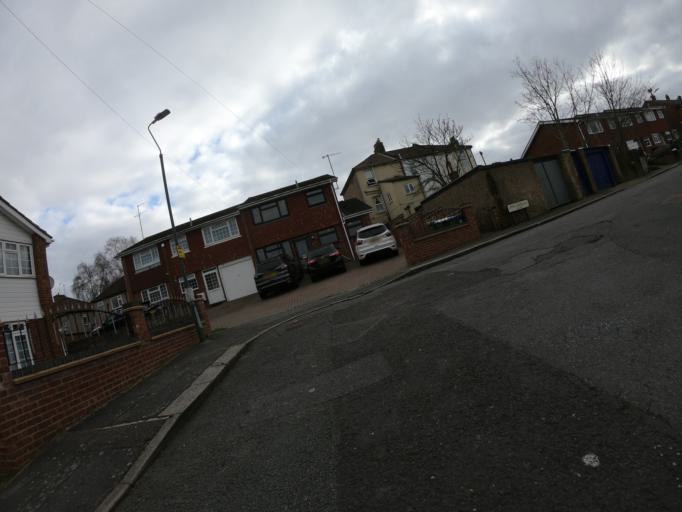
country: GB
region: England
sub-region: Greater London
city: Belvedere
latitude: 51.4894
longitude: 0.1477
